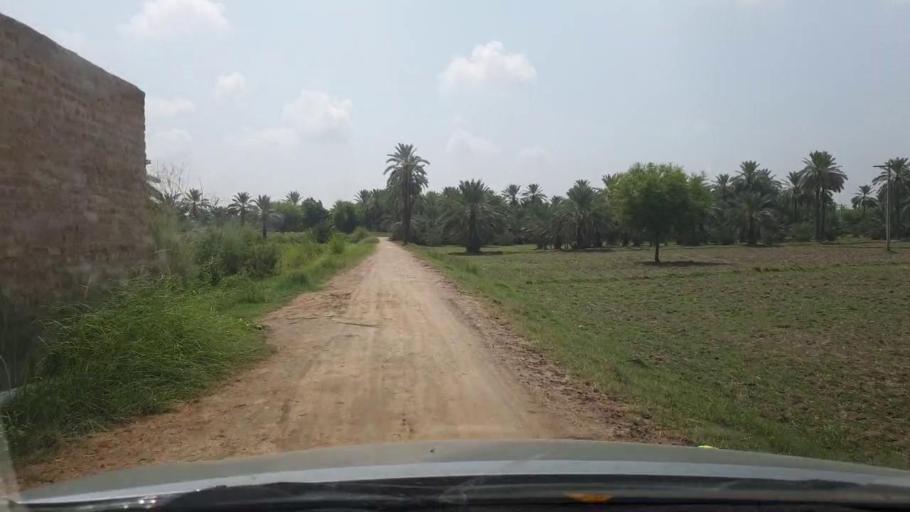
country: PK
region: Sindh
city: Khairpur
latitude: 27.4837
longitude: 68.7331
